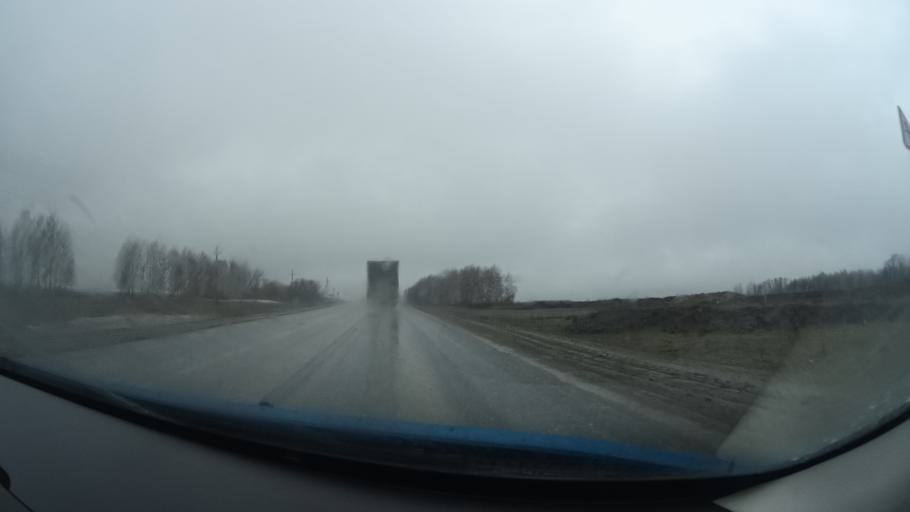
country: RU
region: Bashkortostan
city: Buzdyak
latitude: 54.6933
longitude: 54.8220
